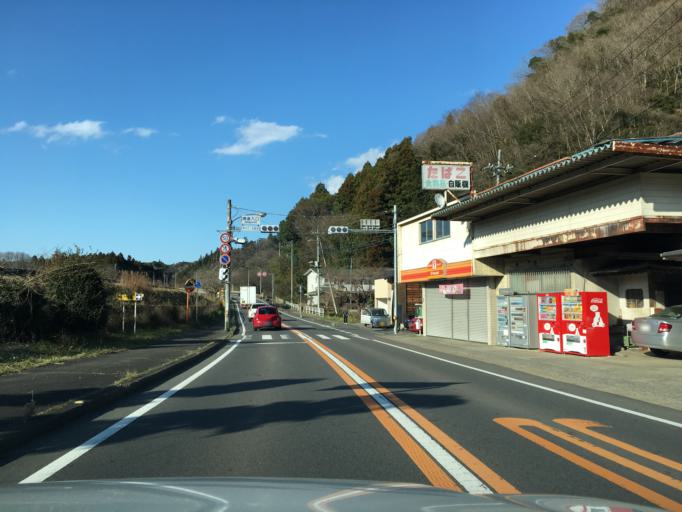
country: JP
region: Ibaraki
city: Daigo
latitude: 36.7120
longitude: 140.3865
